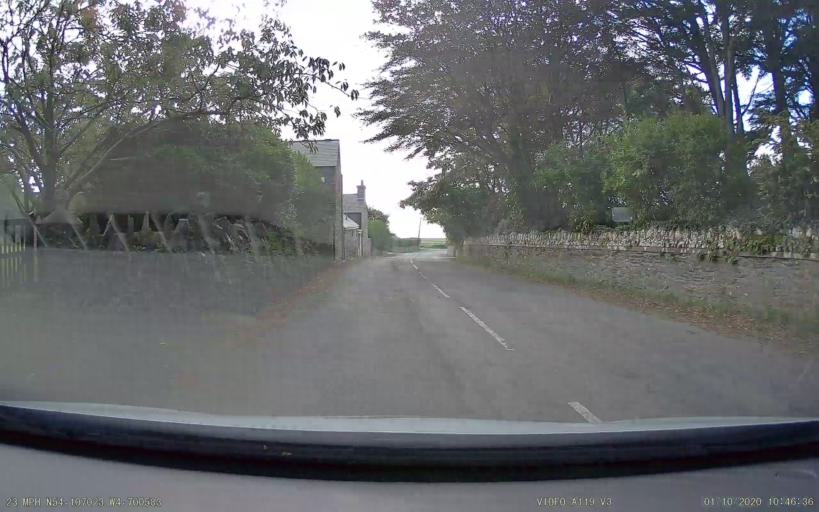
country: IM
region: Port Erin
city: Port Erin
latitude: 54.1070
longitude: -4.7006
